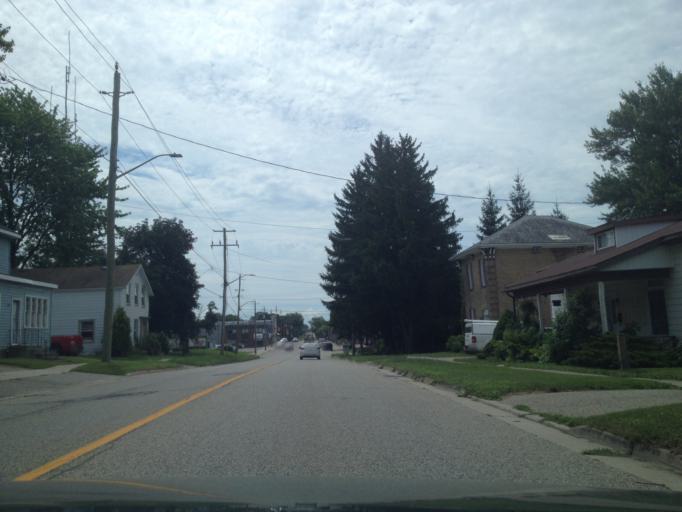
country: CA
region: Ontario
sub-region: Oxford County
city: Woodstock
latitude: 42.9901
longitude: -80.5982
